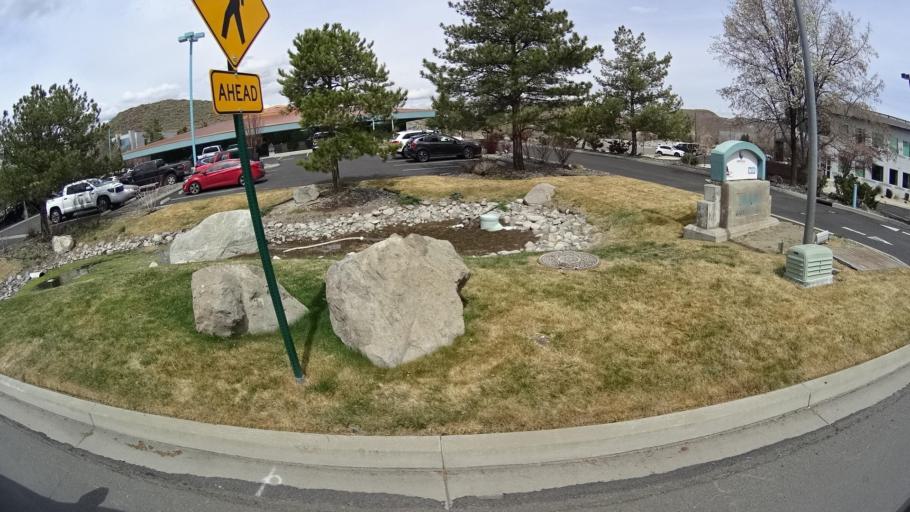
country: US
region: Nevada
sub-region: Washoe County
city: Sparks
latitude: 39.4460
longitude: -119.7651
